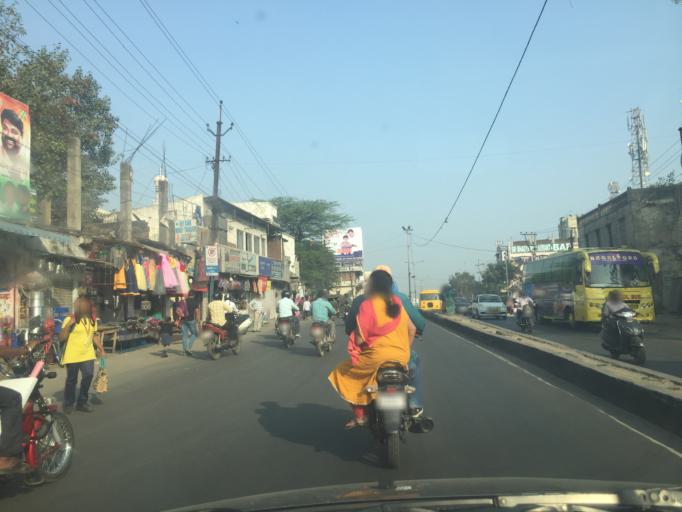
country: IN
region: Telangana
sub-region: Rangareddi
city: Uppal Kalan
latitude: 17.4015
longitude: 78.5652
